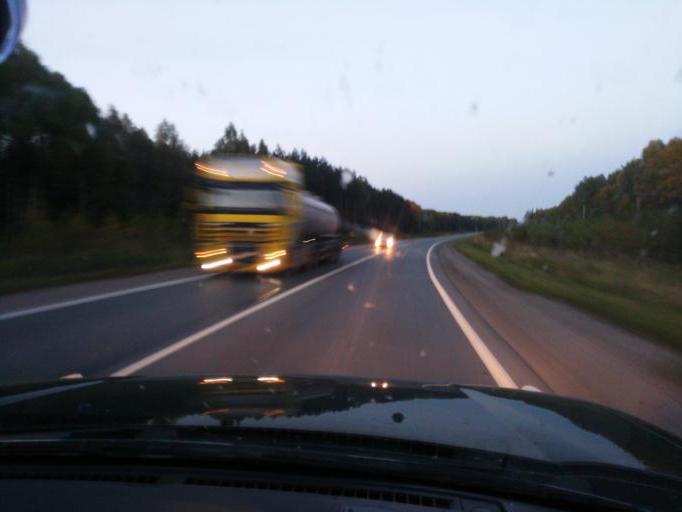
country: RU
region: Perm
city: Verkhnechusovskiye Gorodki
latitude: 58.2383
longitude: 57.2219
